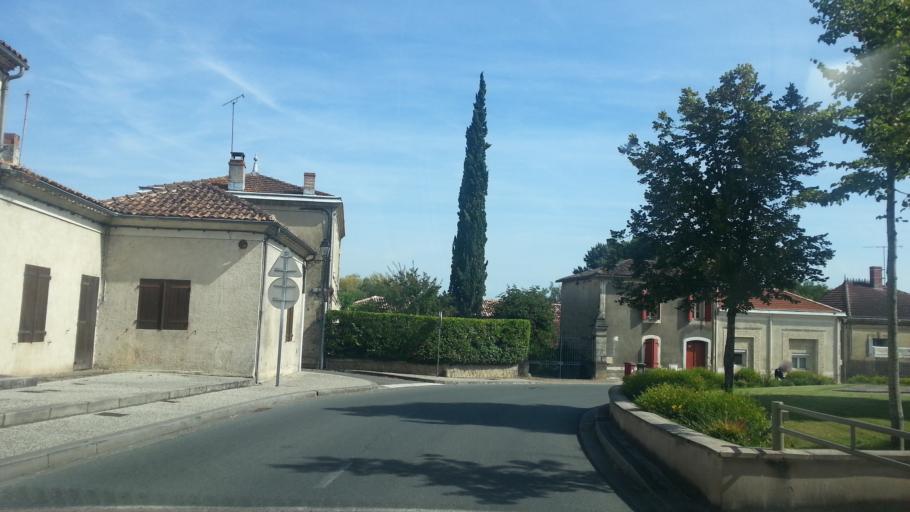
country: FR
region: Aquitaine
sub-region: Departement de la Gironde
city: Illats
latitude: 44.5976
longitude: -0.3732
